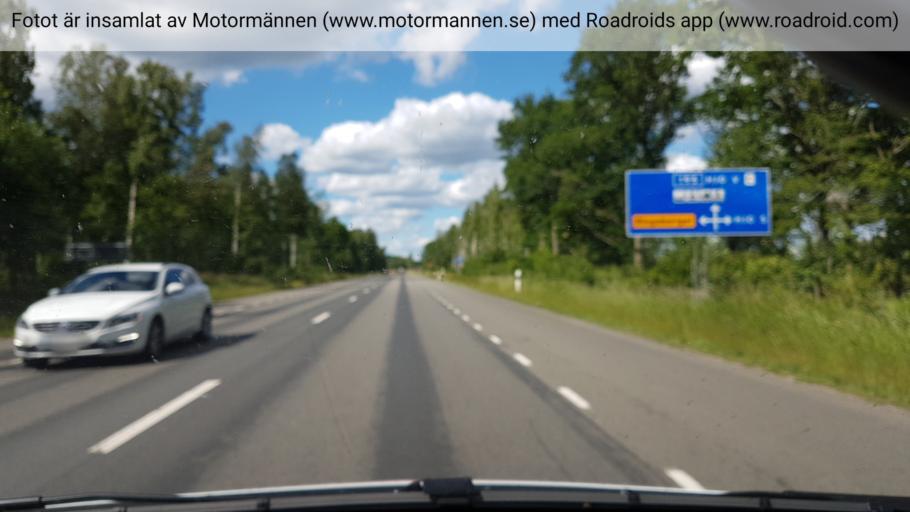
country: SE
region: Vaestra Goetaland
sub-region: Hjo Kommun
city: Hjo
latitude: 58.2854
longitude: 14.2615
